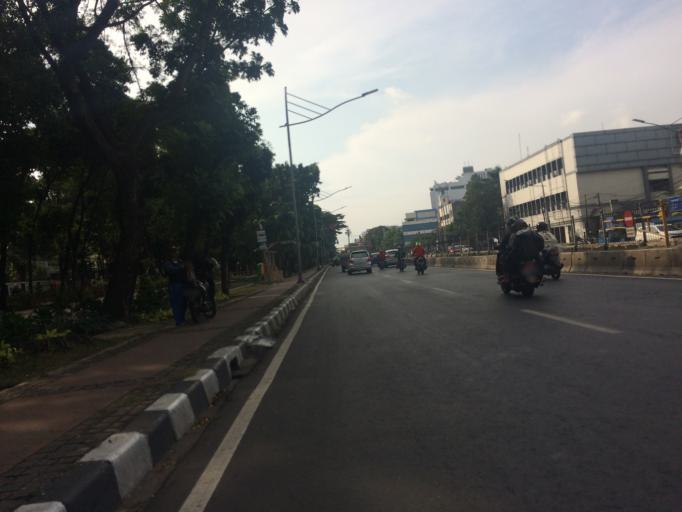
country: ID
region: Jakarta Raya
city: Jakarta
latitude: -6.1703
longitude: 106.8385
